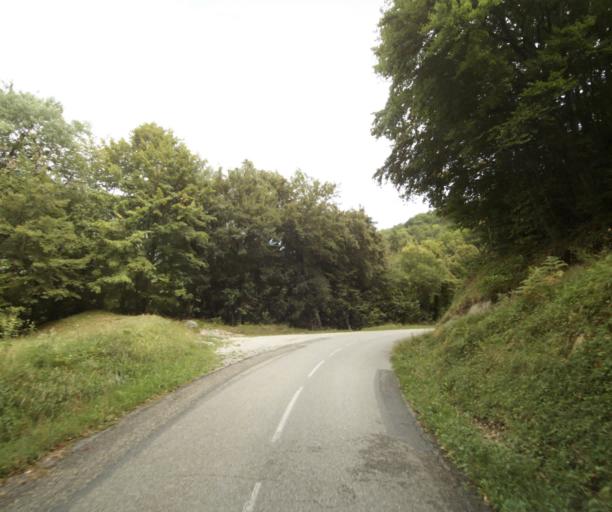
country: FR
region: Rhone-Alpes
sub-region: Departement de l'Isere
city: Saint-Egreve
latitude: 45.2670
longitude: 5.7083
